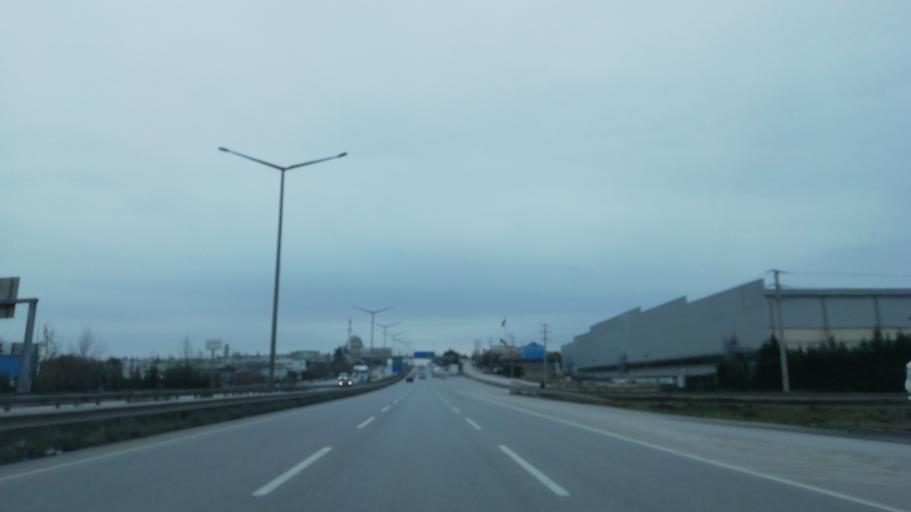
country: TR
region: Kocaeli
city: Gebze
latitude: 40.8005
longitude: 29.4622
